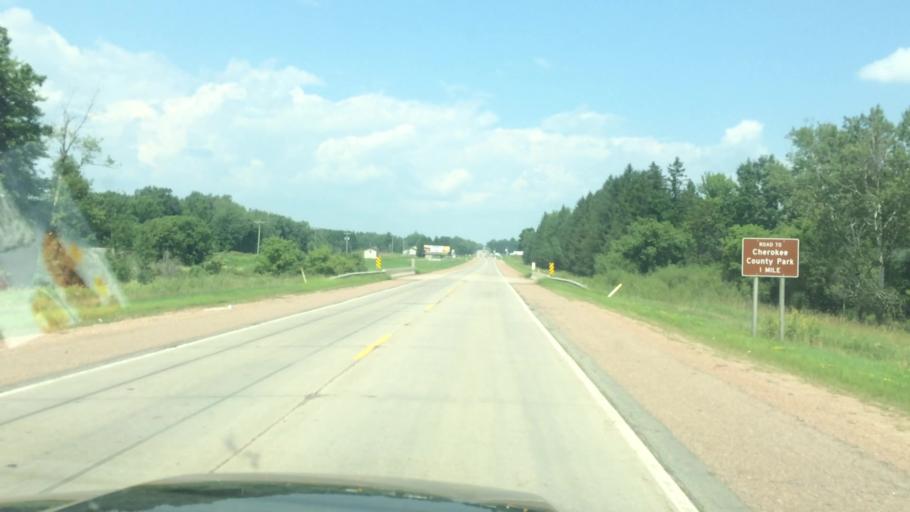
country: US
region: Wisconsin
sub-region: Clark County
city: Colby
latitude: 44.8882
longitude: -90.3153
